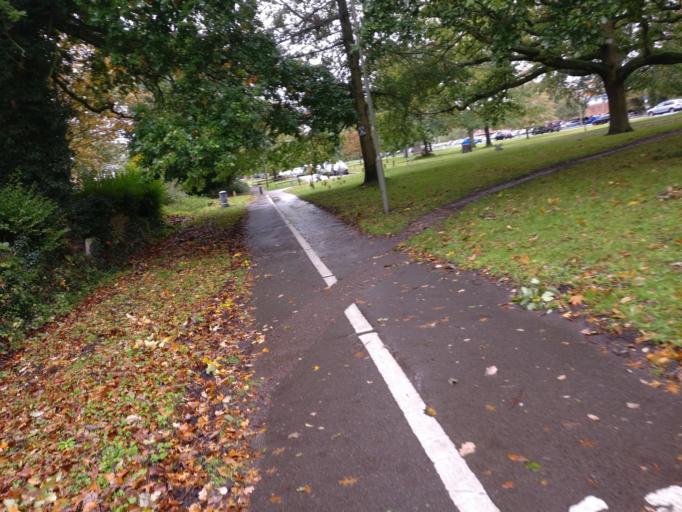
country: GB
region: England
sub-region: Surrey
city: Frimley
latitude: 51.3185
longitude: -0.7380
